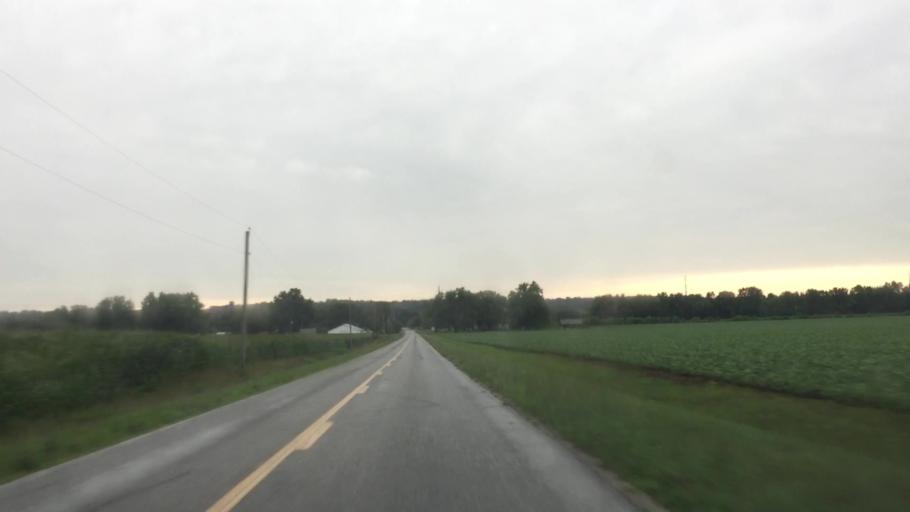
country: US
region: Iowa
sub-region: Lee County
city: Fort Madison
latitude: 40.6126
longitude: -91.2819
